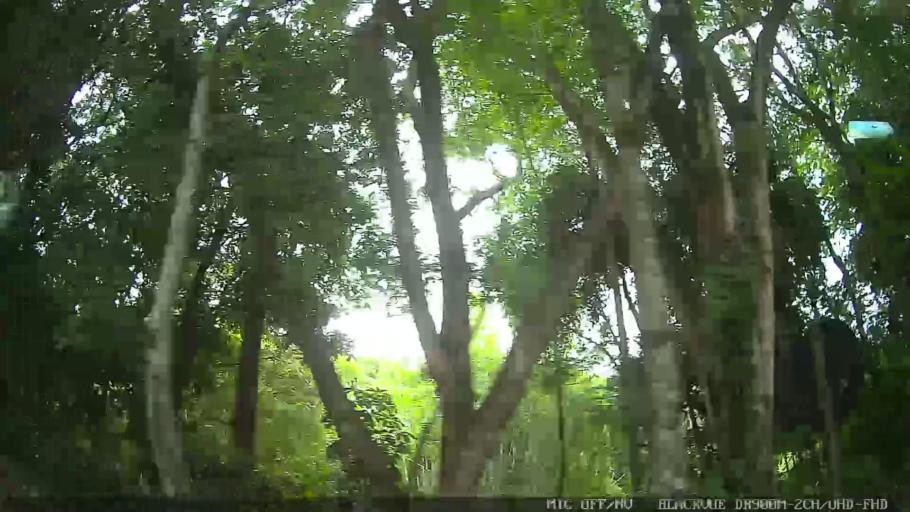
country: BR
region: Sao Paulo
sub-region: Pedreira
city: Pedreira
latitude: -22.7430
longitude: -46.9189
